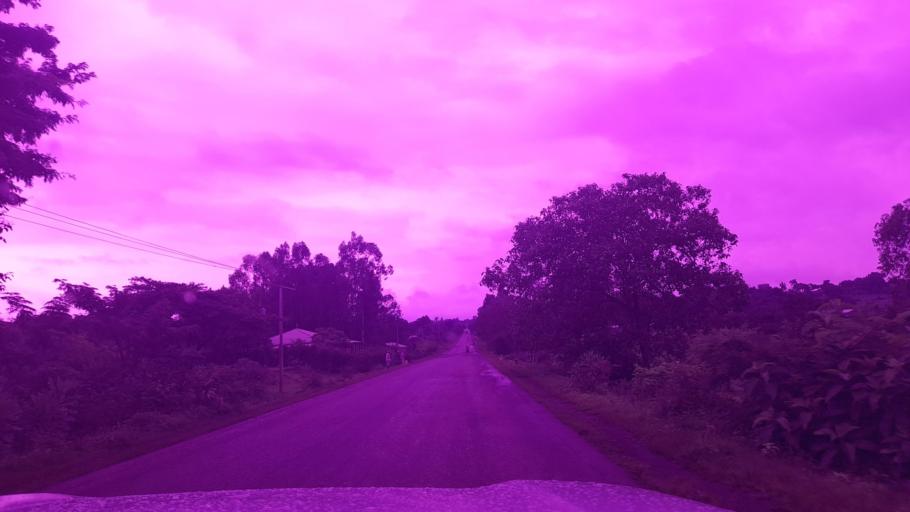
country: ET
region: Oromiya
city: Jima
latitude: 7.7074
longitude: 37.2527
